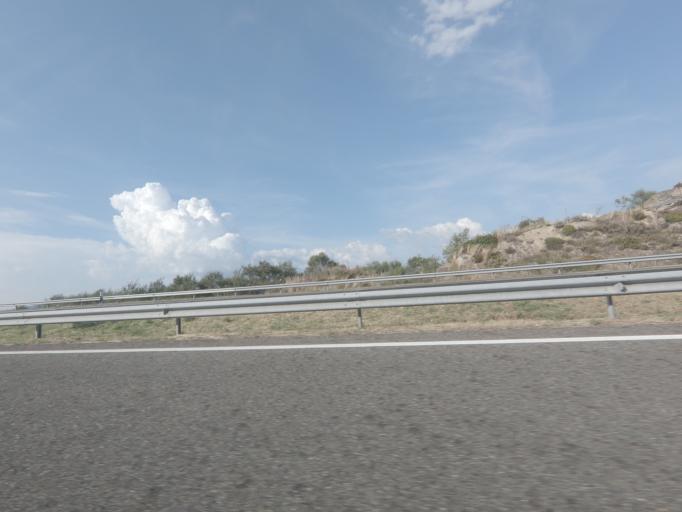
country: ES
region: Galicia
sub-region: Provincia de Ourense
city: Verin
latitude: 41.9491
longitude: -7.5062
